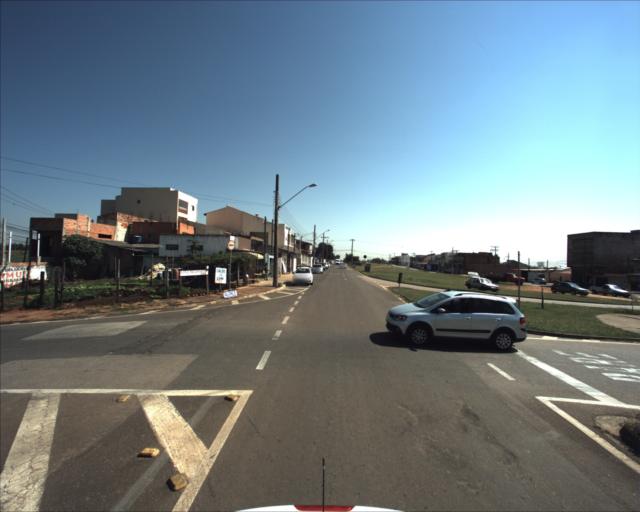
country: BR
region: Sao Paulo
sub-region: Sorocaba
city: Sorocaba
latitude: -23.4967
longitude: -47.5297
